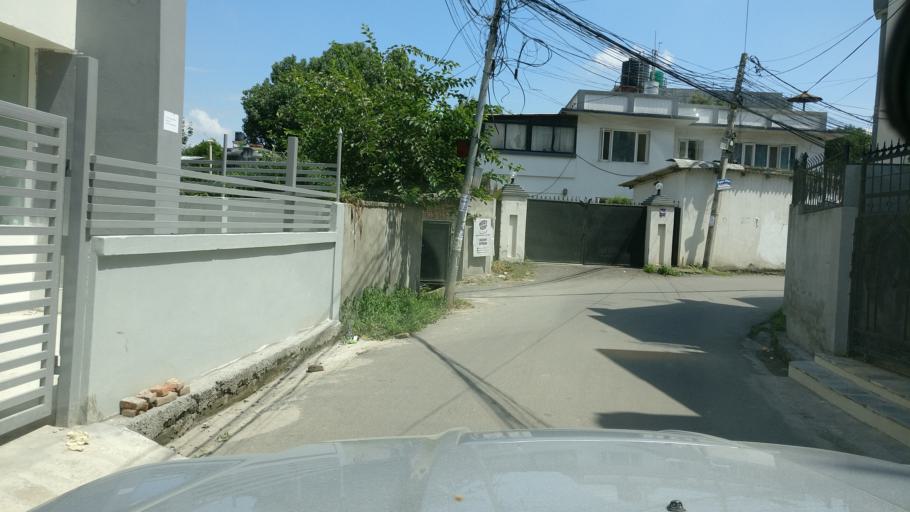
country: NP
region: Central Region
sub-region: Bagmati Zone
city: Patan
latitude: 27.6839
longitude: 85.3083
